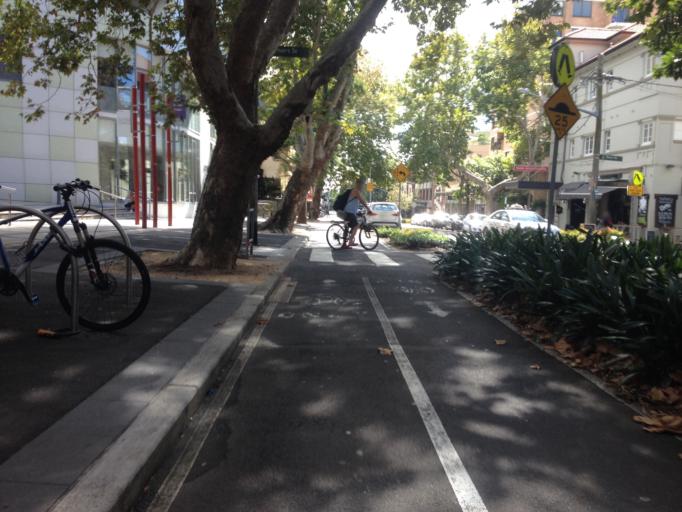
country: AU
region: New South Wales
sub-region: City of Sydney
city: Darlinghurst
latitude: -33.8828
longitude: 151.2164
